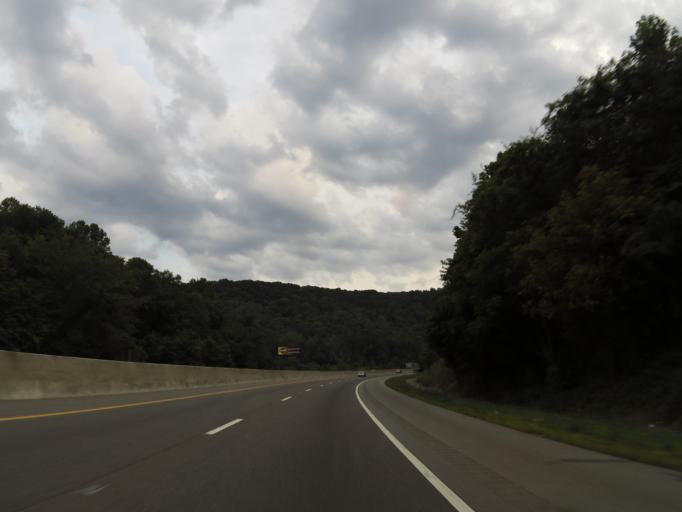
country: US
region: Tennessee
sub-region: Anderson County
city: Norris
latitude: 36.0926
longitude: -84.0122
